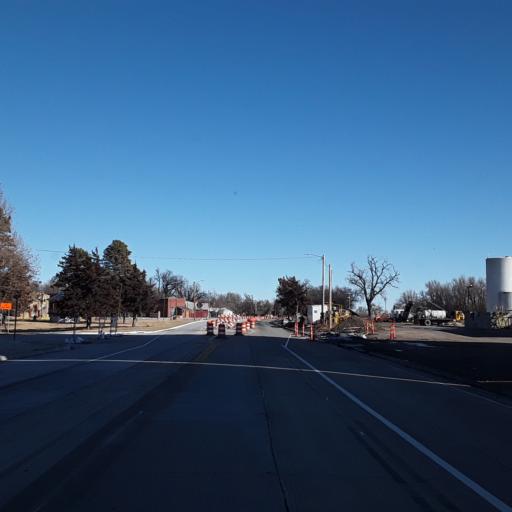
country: US
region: Kansas
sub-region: Pawnee County
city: Larned
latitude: 38.0743
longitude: -99.2445
